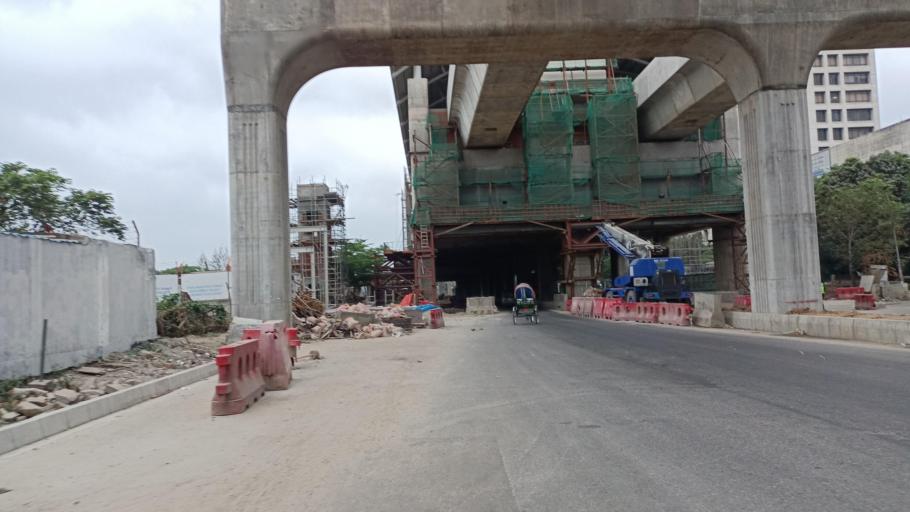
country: BD
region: Dhaka
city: Azimpur
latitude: 23.7797
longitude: 90.3798
